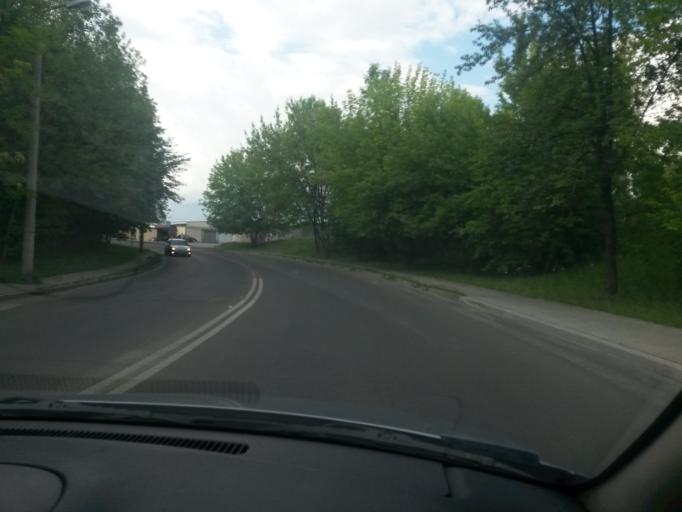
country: PL
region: Silesian Voivodeship
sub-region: Dabrowa Gornicza
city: Dabrowa Gornicza
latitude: 50.3177
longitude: 19.2073
